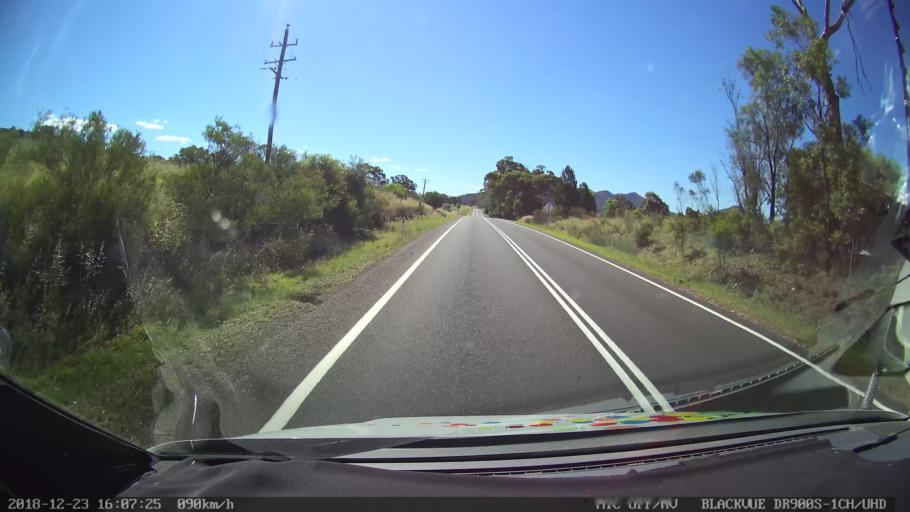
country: AU
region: New South Wales
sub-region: Tamworth Municipality
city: Phillip
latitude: -31.2715
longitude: 150.7625
